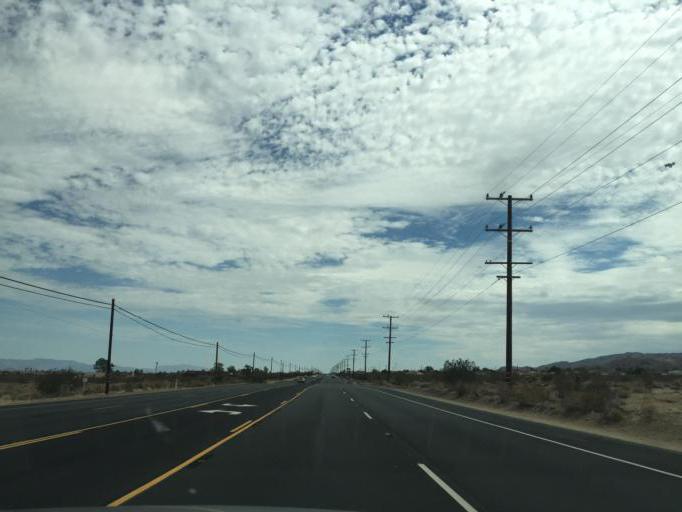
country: US
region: California
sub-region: San Bernardino County
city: Twentynine Palms
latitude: 34.1351
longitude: -116.1657
